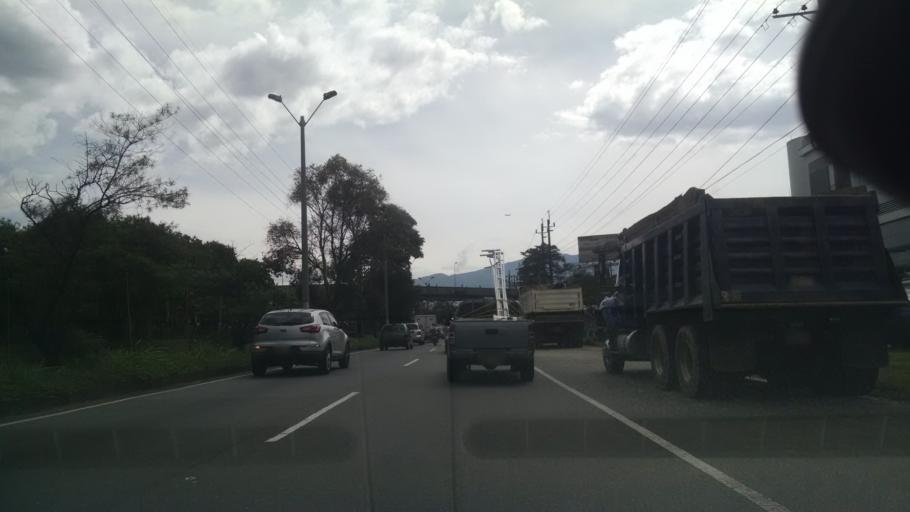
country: CO
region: Antioquia
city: Envigado
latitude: 6.1877
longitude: -75.5848
